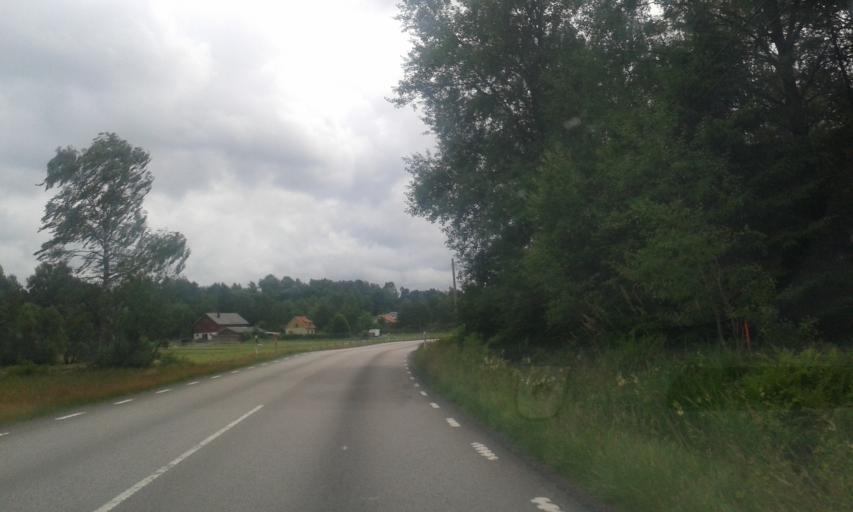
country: SE
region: Vaestra Goetaland
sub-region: Kungalvs Kommun
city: Kode
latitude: 57.8910
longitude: 11.8820
